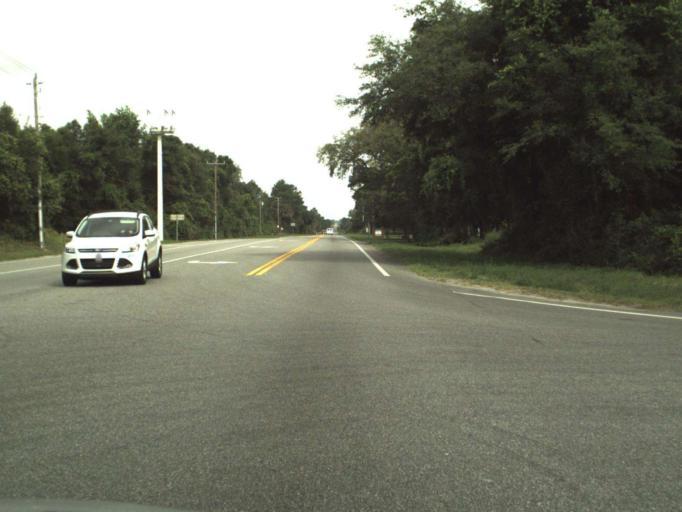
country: US
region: Florida
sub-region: Seminole County
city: Geneva
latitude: 28.7415
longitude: -81.1241
